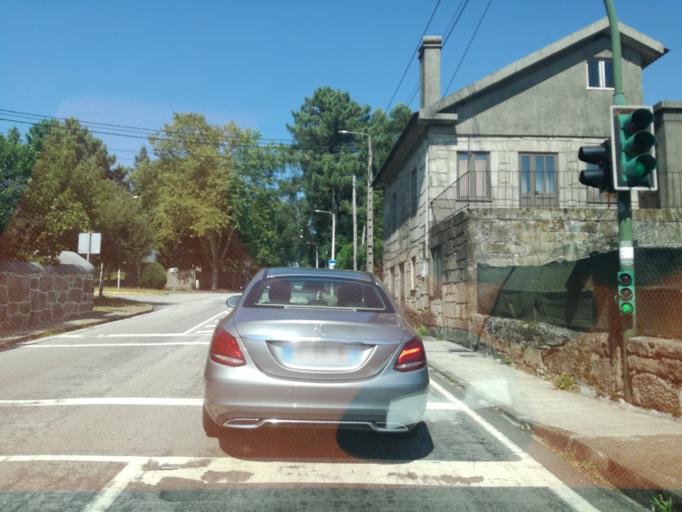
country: PT
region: Viana do Castelo
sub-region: Viana do Castelo
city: Darque
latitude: 41.6669
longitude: -8.7834
